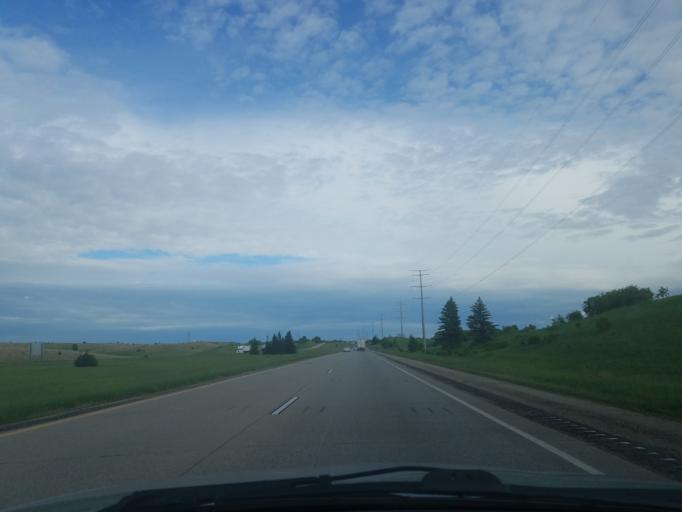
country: US
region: Minnesota
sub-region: Otter Tail County
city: Fergus Falls
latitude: 46.2400
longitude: -96.0589
